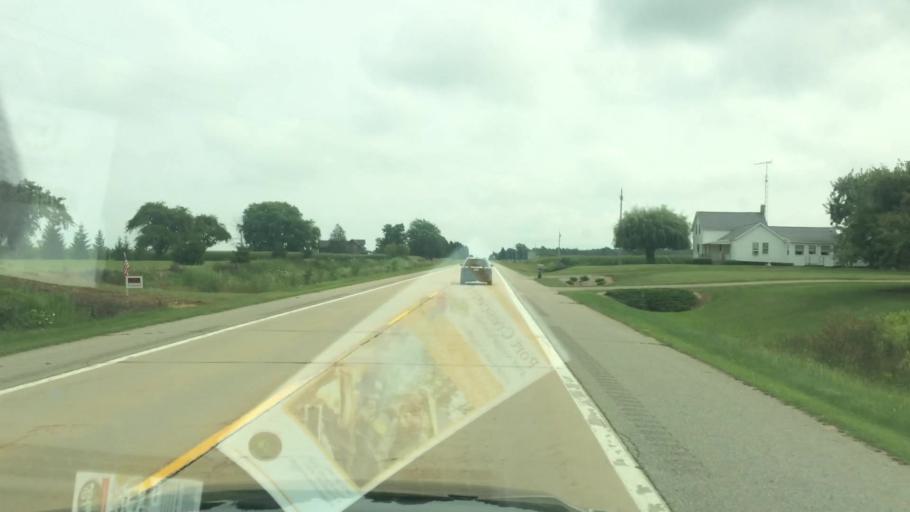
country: US
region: Michigan
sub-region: Huron County
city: Bad Axe
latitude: 44.0427
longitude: -82.9371
